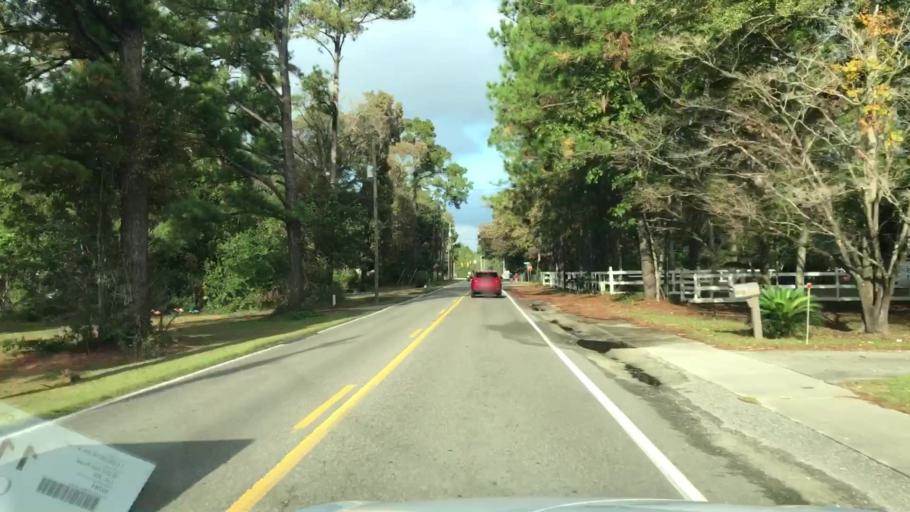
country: US
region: South Carolina
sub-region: Berkeley County
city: Sangaree
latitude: 33.0291
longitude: -80.1134
